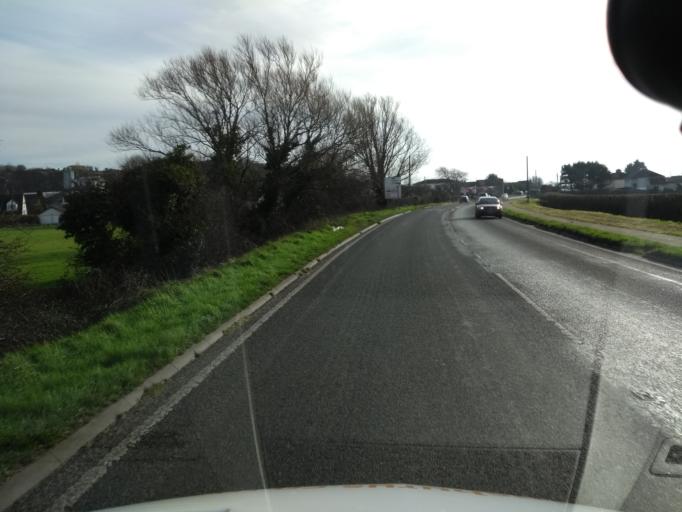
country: GB
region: England
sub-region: North Somerset
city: Bleadon
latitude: 51.3050
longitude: -2.9505
